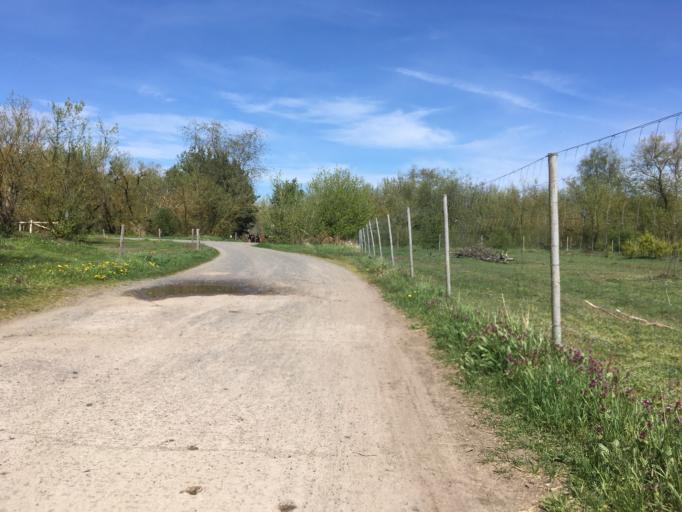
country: DE
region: Berlin
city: Buch
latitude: 52.6672
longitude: 13.4907
